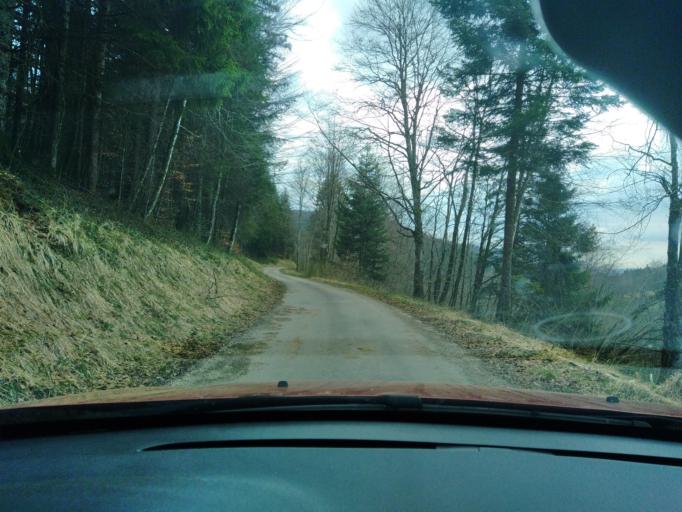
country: FR
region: Franche-Comte
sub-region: Departement du Jura
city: Moirans-en-Montagne
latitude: 46.4583
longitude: 5.7605
